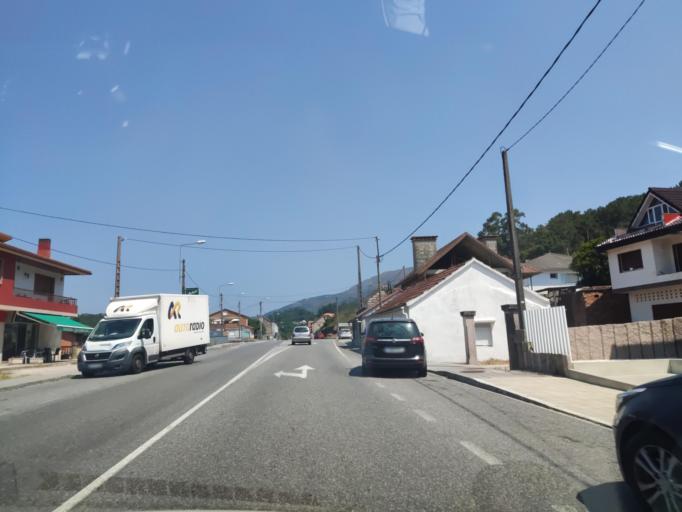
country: ES
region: Galicia
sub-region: Provincia de Pontevedra
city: Porrino
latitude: 42.2026
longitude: -8.6028
